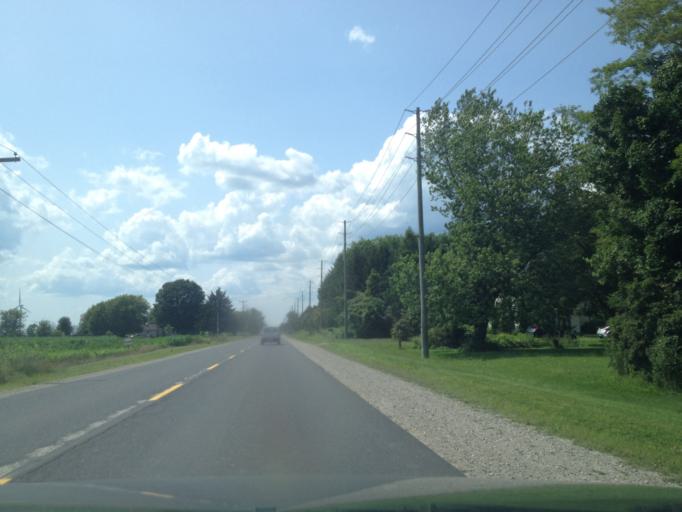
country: CA
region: Ontario
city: Aylmer
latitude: 42.6638
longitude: -80.8196
